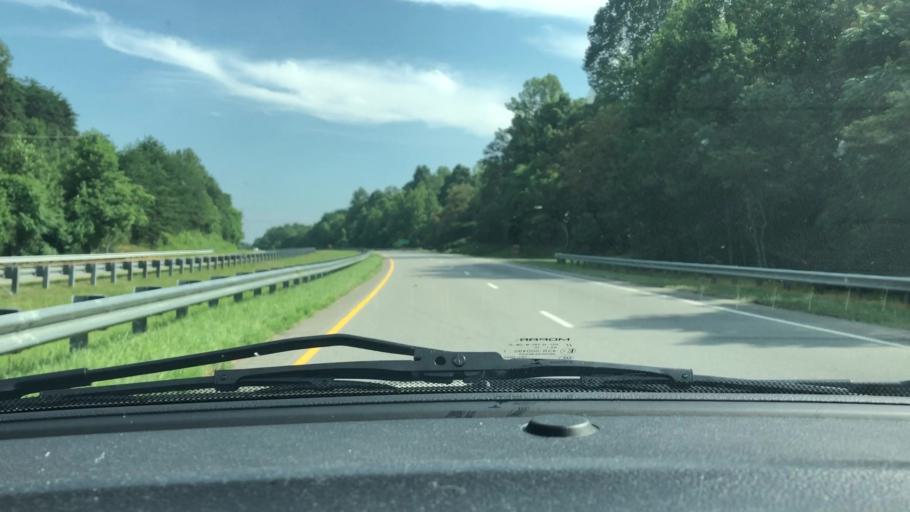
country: US
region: North Carolina
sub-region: Rockingham County
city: Stoneville
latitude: 36.5246
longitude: -79.9175
